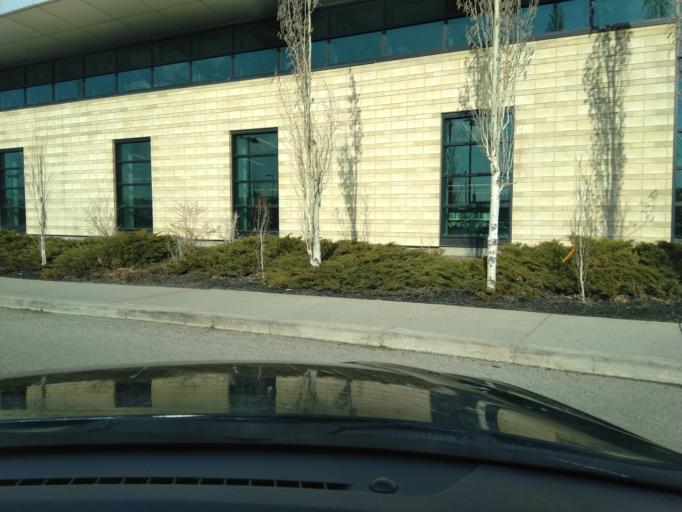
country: CA
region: Alberta
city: Calgary
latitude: 51.1589
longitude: -114.0668
